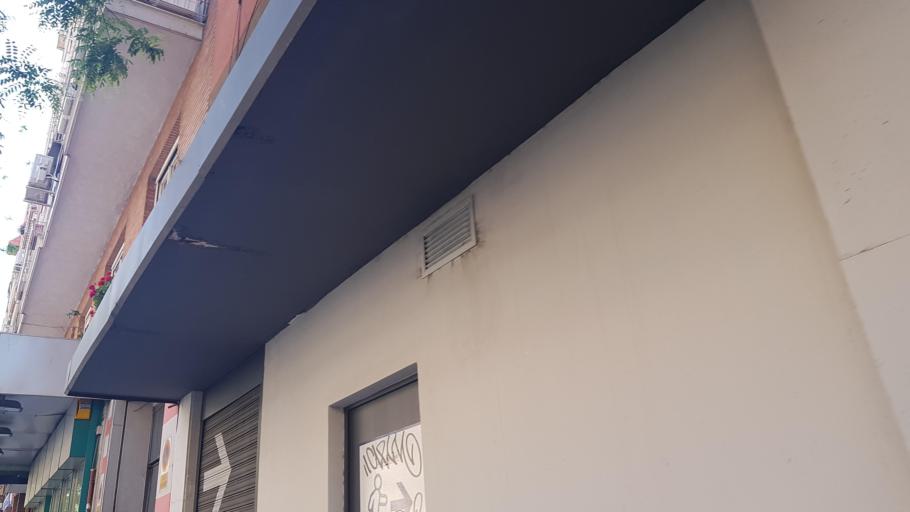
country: ES
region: Madrid
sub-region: Provincia de Madrid
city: Moratalaz
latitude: 40.4339
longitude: -3.6560
